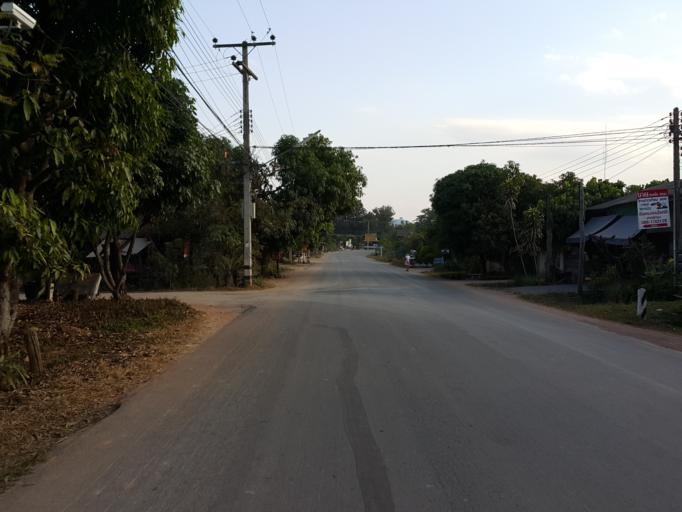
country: TH
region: Lamphun
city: Thung Hua Chang
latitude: 18.0108
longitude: 99.0262
